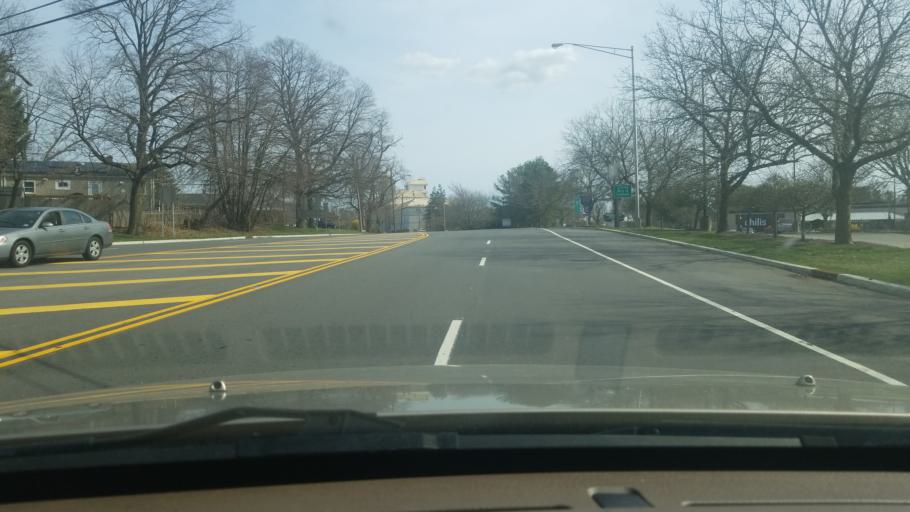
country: US
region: New Jersey
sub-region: Monmouth County
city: Freehold
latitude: 40.2584
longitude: -74.2899
